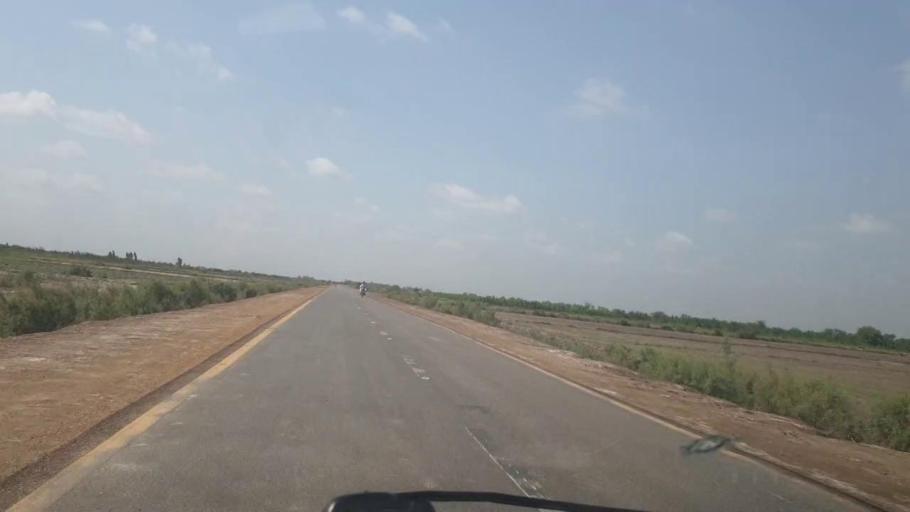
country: PK
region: Sindh
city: Berani
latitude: 25.7197
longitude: 68.9449
